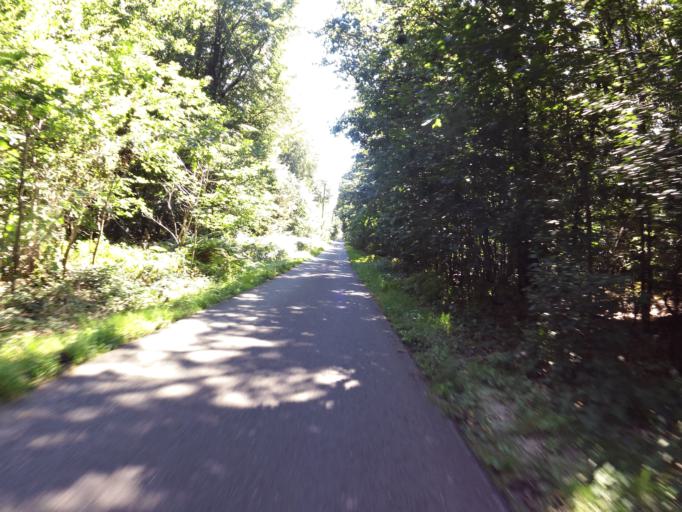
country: DE
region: North Rhine-Westphalia
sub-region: Regierungsbezirk Dusseldorf
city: Kranenburg
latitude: 51.7684
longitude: 6.0055
